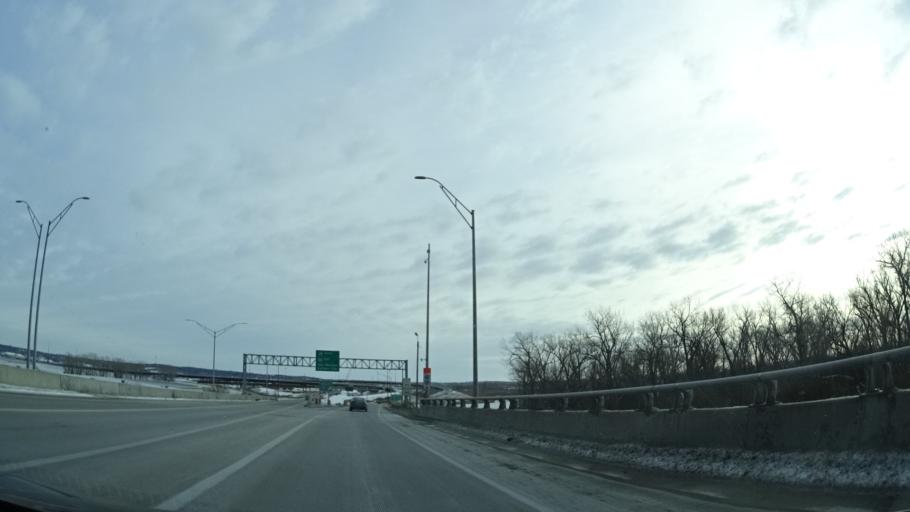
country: US
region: Nebraska
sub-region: Douglas County
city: Omaha
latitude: 41.2318
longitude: -95.9077
